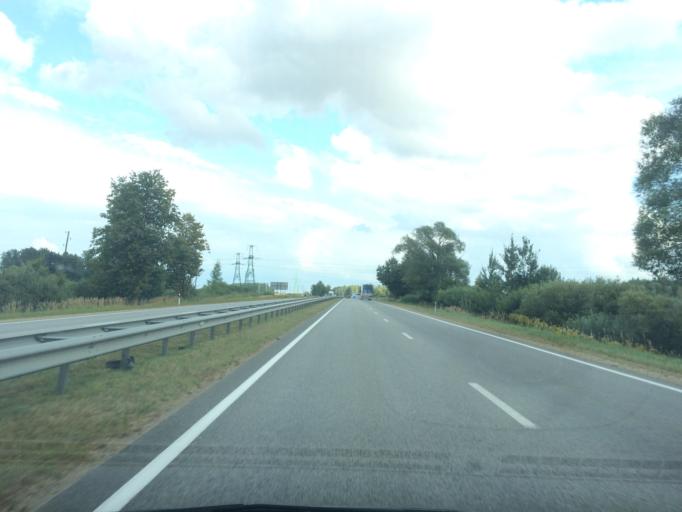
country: LV
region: Salaspils
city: Salaspils
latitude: 56.8463
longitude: 24.3700
